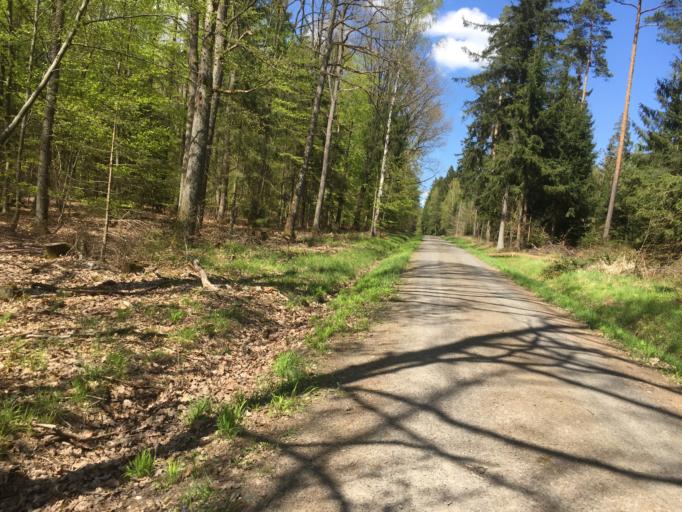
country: DE
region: Bavaria
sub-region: Regierungsbezirk Unterfranken
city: Sulzfeld
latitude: 50.2336
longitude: 10.4319
